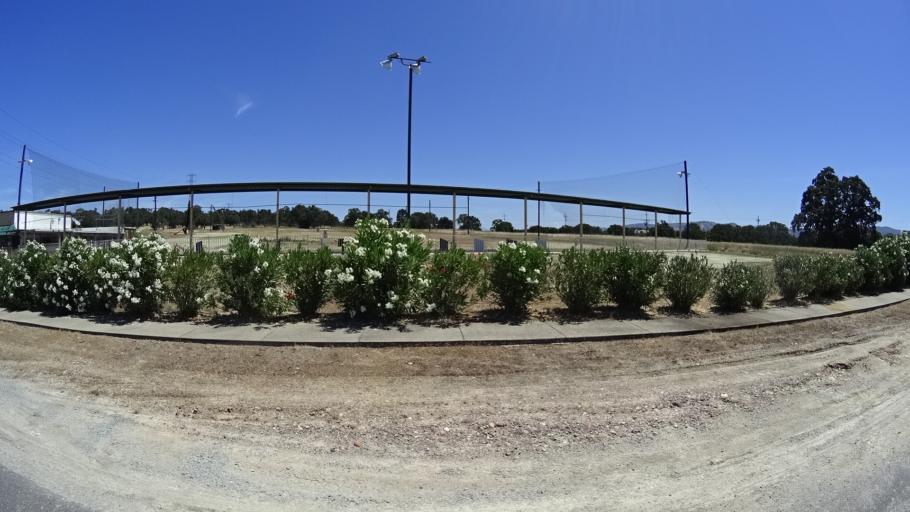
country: US
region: California
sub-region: Calaveras County
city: Valley Springs
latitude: 38.1718
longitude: -120.8390
